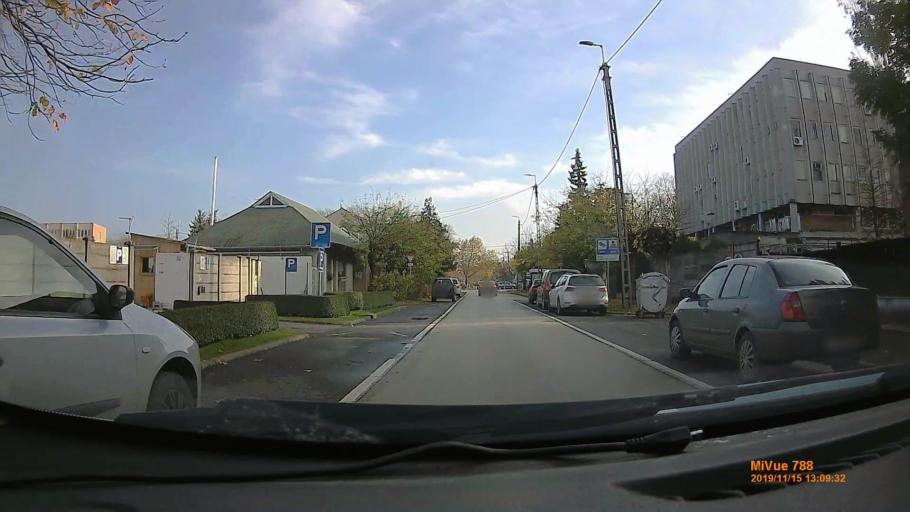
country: HU
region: Bekes
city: Gyula
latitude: 46.6416
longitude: 21.2779
